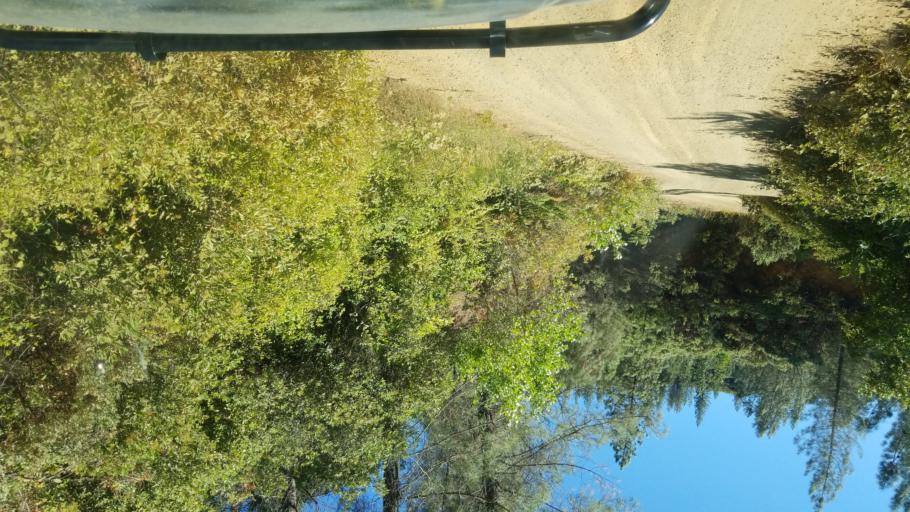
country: US
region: California
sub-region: Shasta County
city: Shasta
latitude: 40.6624
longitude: -122.4643
